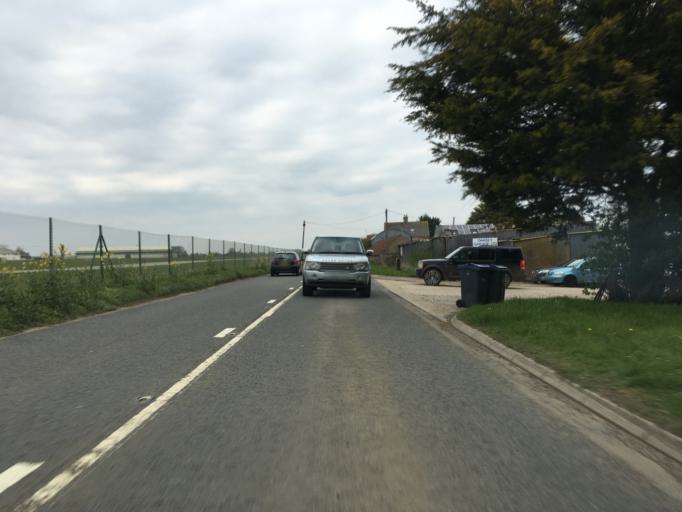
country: GB
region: England
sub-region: Gloucestershire
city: Coates
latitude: 51.6645
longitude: -2.0515
